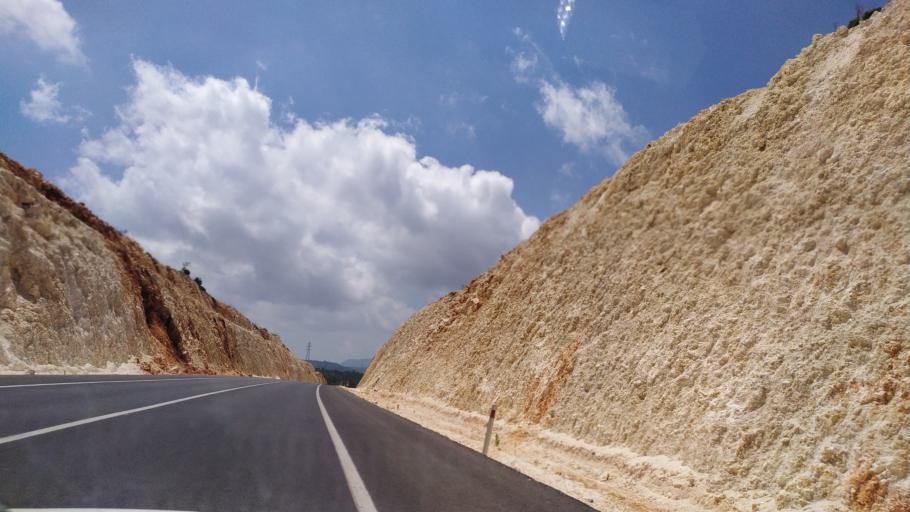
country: TR
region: Mersin
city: Gulnar
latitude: 36.2685
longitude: 33.3705
